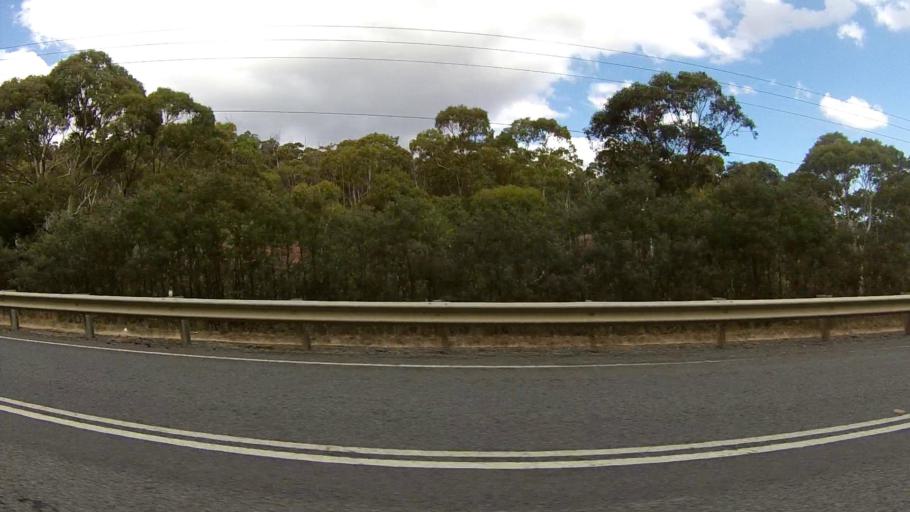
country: AU
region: Tasmania
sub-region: Sorell
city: Sorell
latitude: -42.6328
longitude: 147.6138
